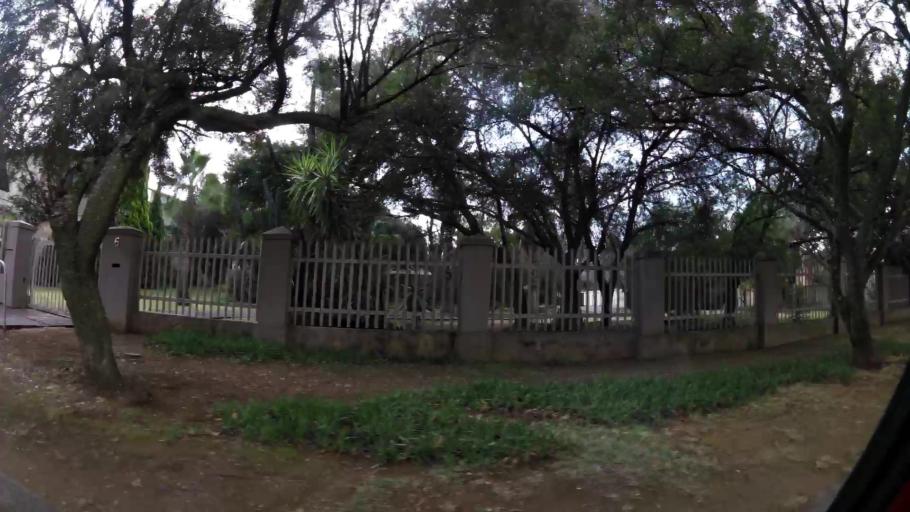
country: ZA
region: Gauteng
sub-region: Sedibeng District Municipality
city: Vanderbijlpark
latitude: -26.7431
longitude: 27.8279
